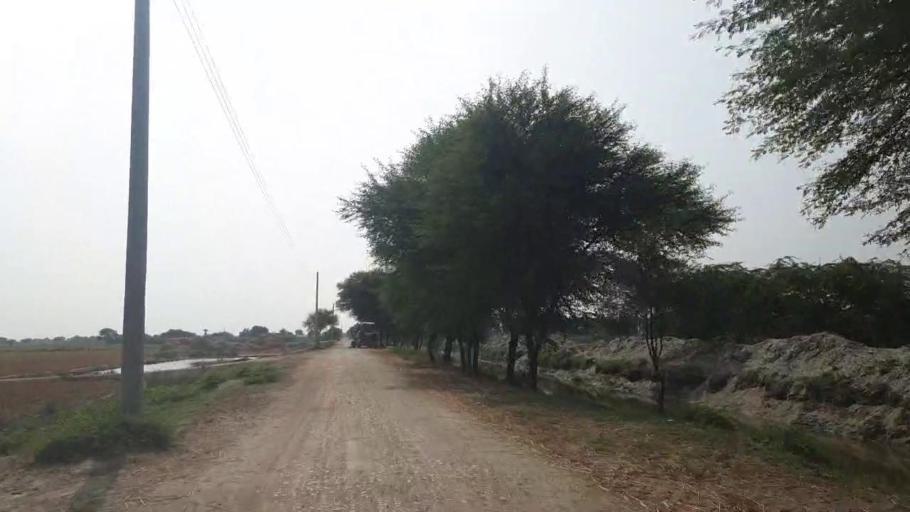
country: PK
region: Sindh
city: Badin
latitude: 24.6168
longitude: 68.7229
